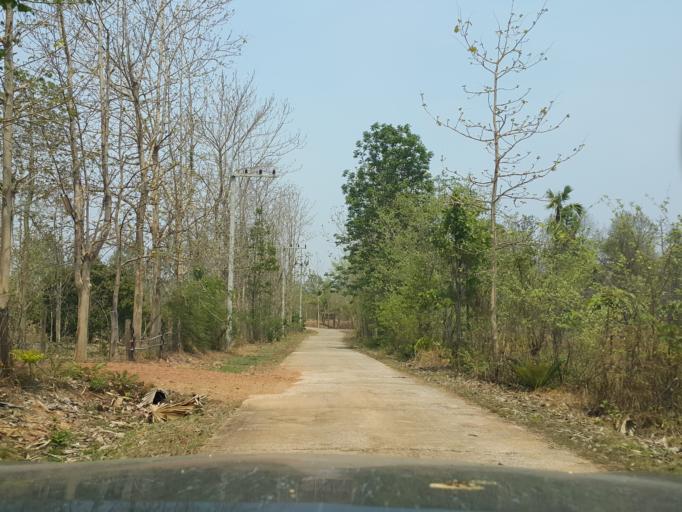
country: TH
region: Lampang
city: Mae Phrik
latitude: 17.5656
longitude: 99.0904
